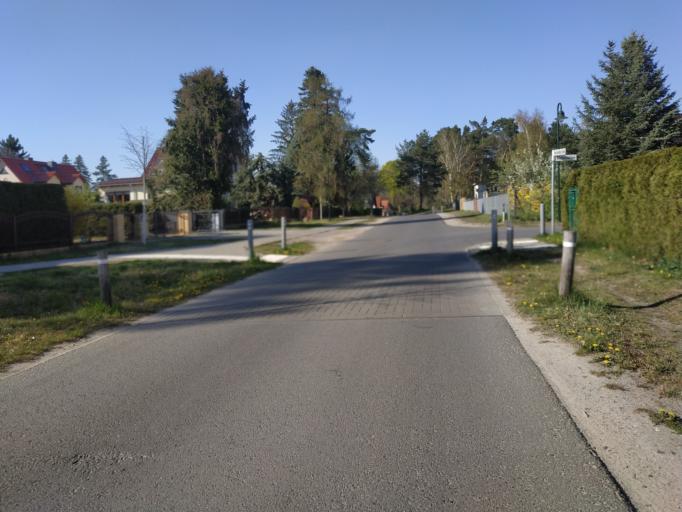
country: DE
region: Brandenburg
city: Petershagen
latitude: 52.5447
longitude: 13.8234
